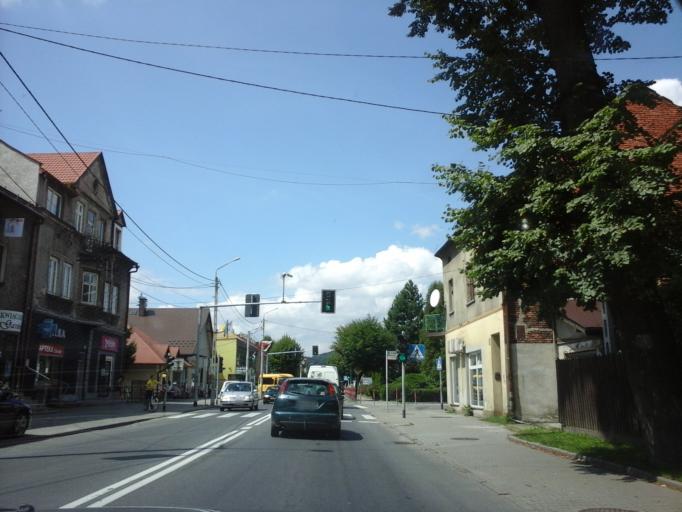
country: PL
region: Lesser Poland Voivodeship
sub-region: Powiat suski
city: Makow Podhalanski
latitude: 49.7286
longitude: 19.6805
